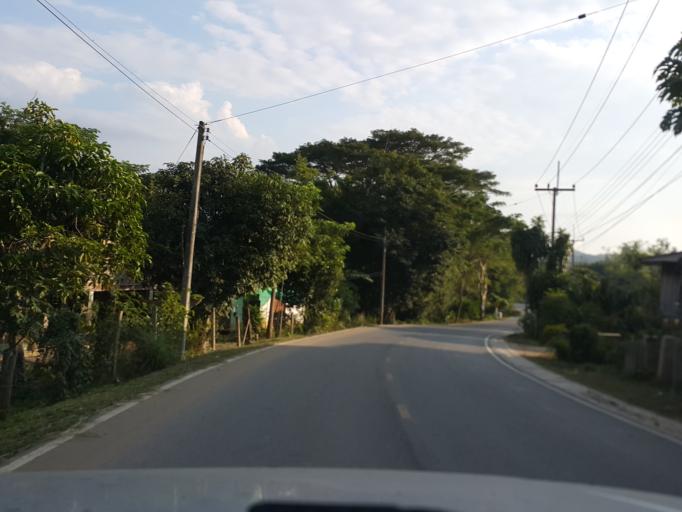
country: TH
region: Chiang Mai
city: Mae On
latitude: 18.6363
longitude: 99.2851
